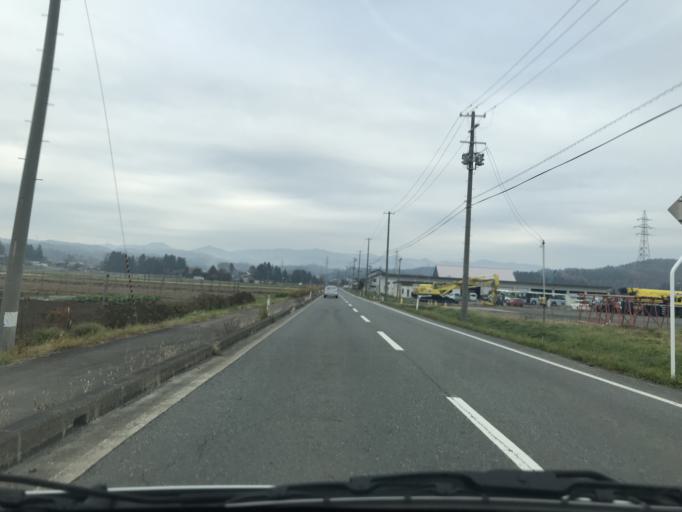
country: JP
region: Iwate
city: Mizusawa
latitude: 39.1599
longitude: 141.1878
